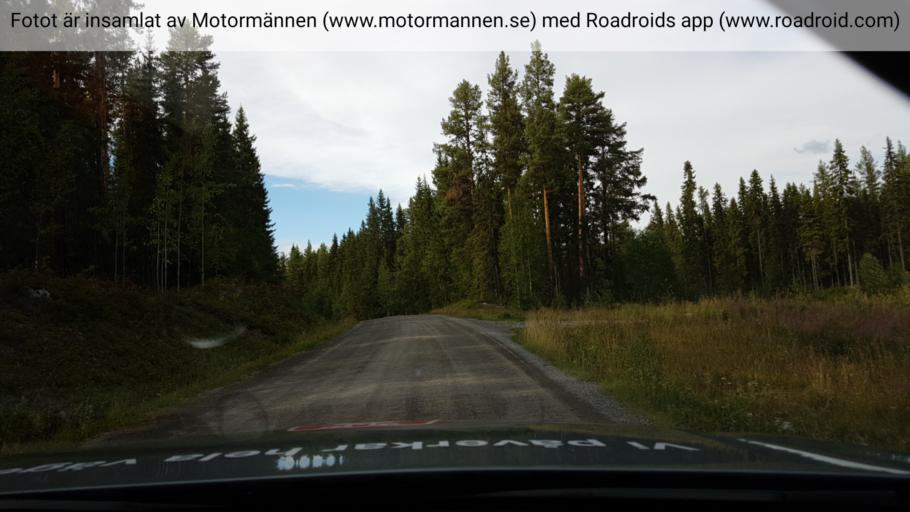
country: SE
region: Jaemtland
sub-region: Braecke Kommun
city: Braecke
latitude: 63.2743
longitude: 15.3760
